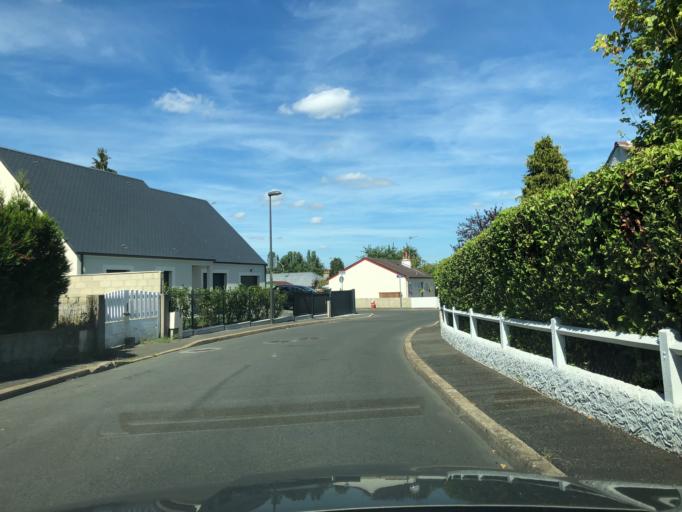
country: FR
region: Centre
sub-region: Departement d'Indre-et-Loire
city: Saint-Cyr-sur-Loire
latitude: 47.4269
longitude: 0.6838
